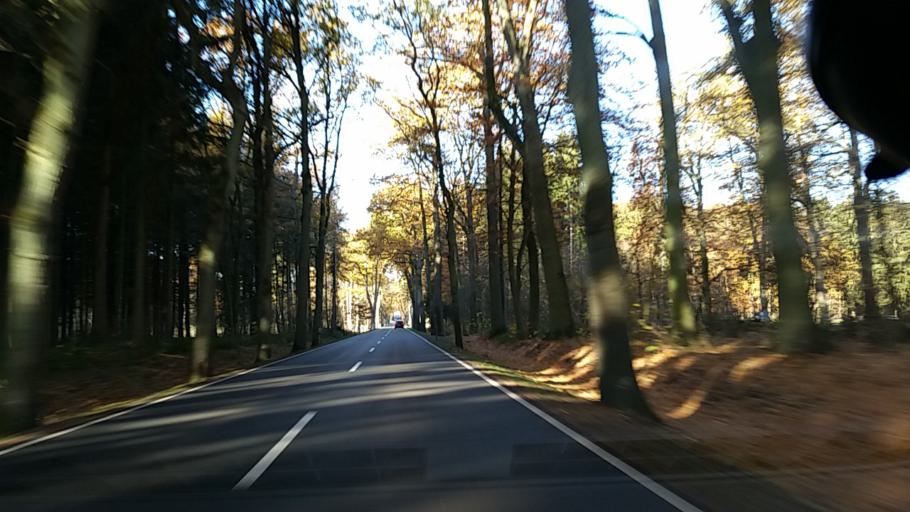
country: DE
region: Saxony-Anhalt
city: Jubar
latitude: 52.6789
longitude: 10.8362
